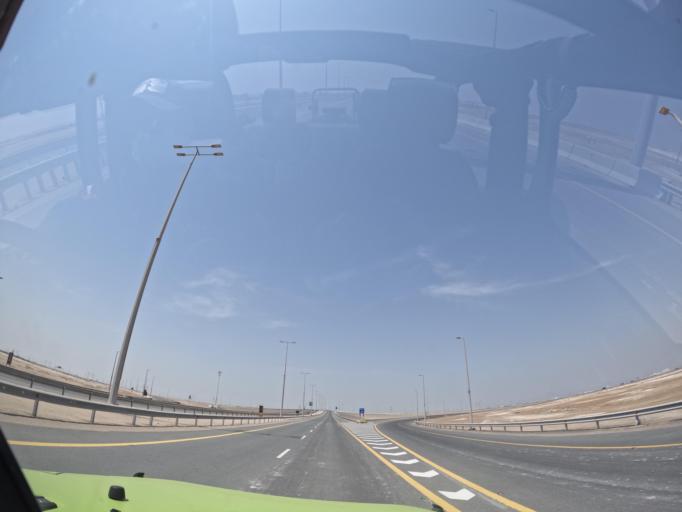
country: AE
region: Abu Dhabi
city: Abu Dhabi
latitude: 24.2428
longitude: 54.4781
